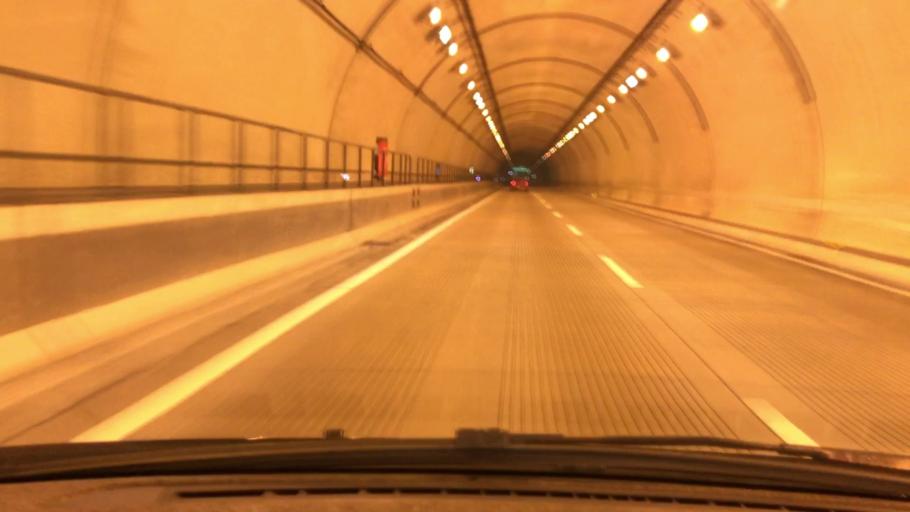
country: JP
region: Hyogo
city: Sandacho
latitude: 34.8249
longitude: 135.2597
